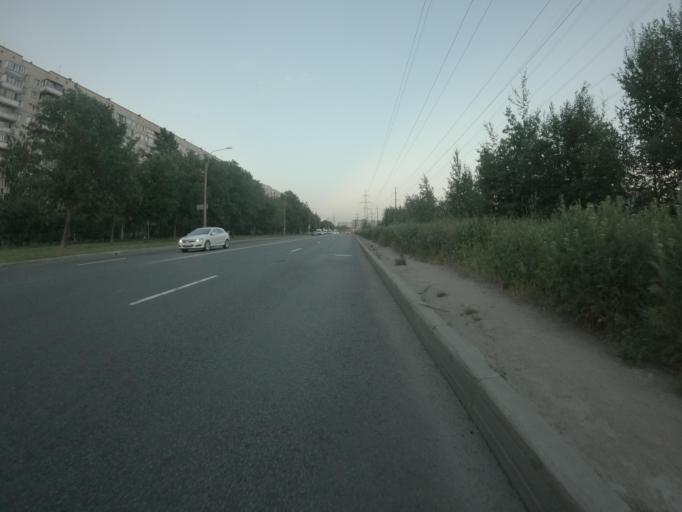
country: RU
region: St.-Petersburg
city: Krasnogvargeisky
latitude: 59.9408
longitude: 30.4663
